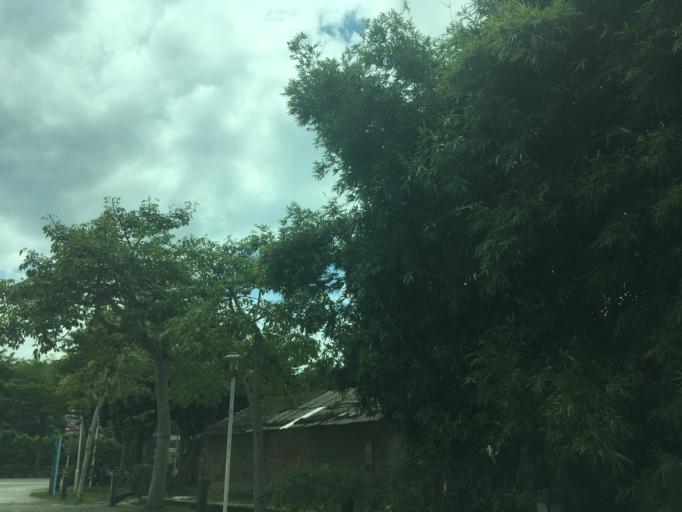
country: TW
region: Taiwan
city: Daxi
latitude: 24.8912
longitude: 121.2954
